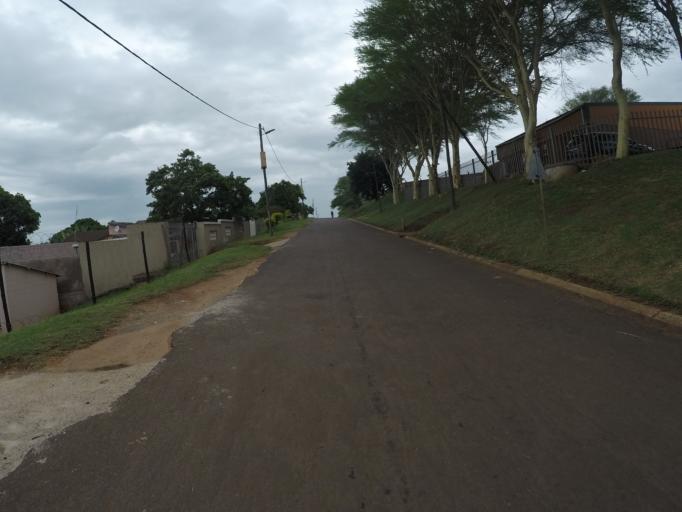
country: ZA
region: KwaZulu-Natal
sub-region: uThungulu District Municipality
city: Empangeni
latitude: -28.7753
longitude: 31.8633
